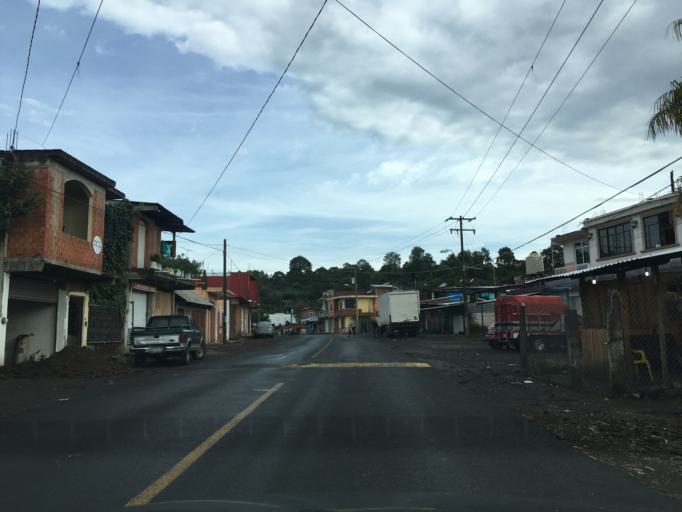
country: MX
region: Michoacan
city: Nuevo San Juan Parangaricutiro
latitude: 19.4235
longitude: -102.1347
